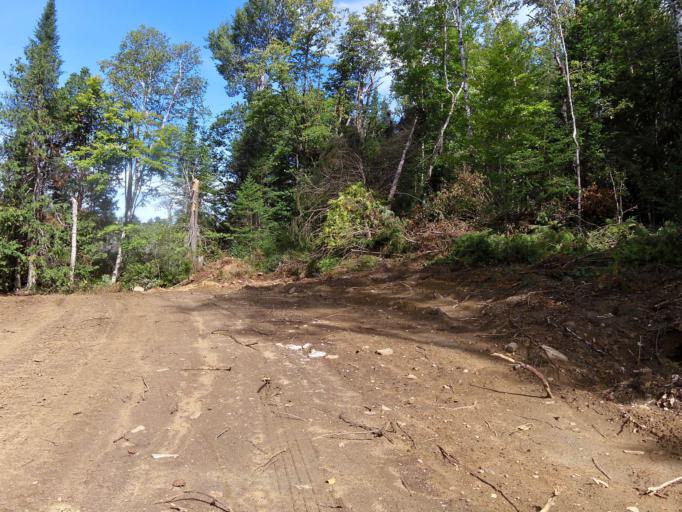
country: CA
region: Ontario
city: Renfrew
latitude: 45.1070
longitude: -76.7214
